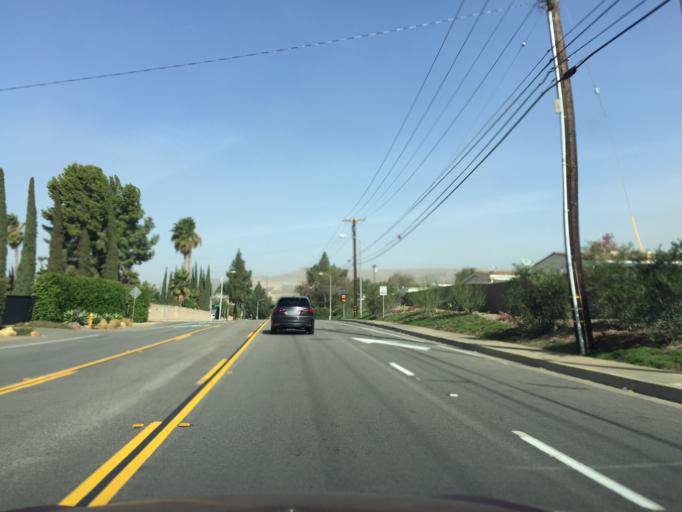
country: US
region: California
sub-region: Orange County
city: Yorba Linda
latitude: 33.9071
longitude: -117.8423
